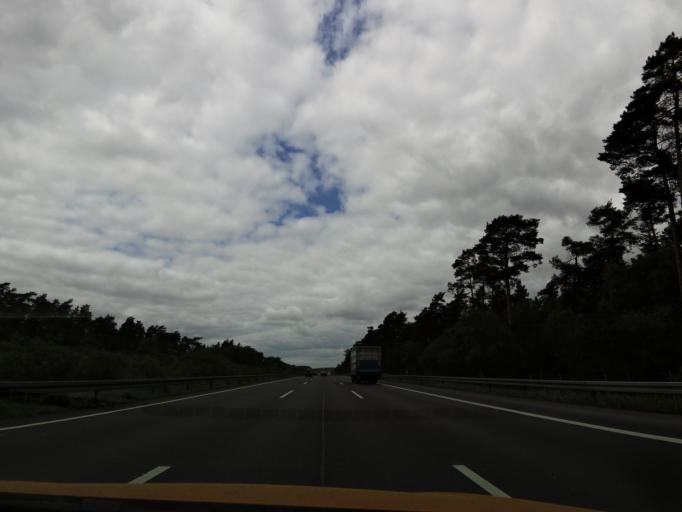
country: DE
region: Lower Saxony
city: Rennau
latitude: 52.2918
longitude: 10.8817
